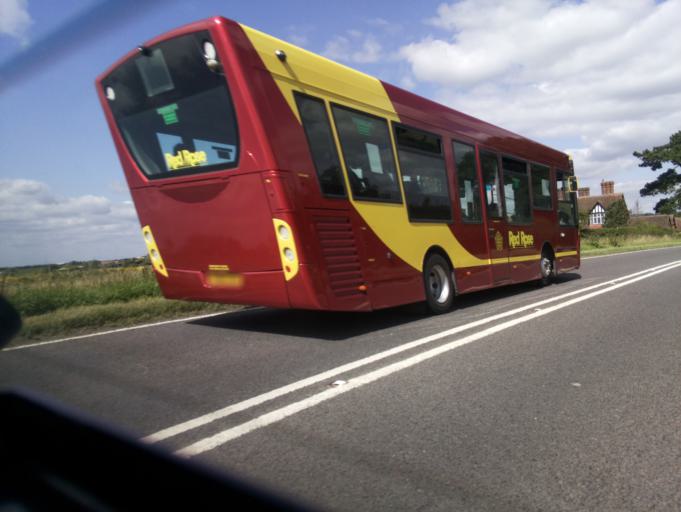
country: GB
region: England
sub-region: Buckinghamshire
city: Aylesbury
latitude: 51.8572
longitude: -0.8300
